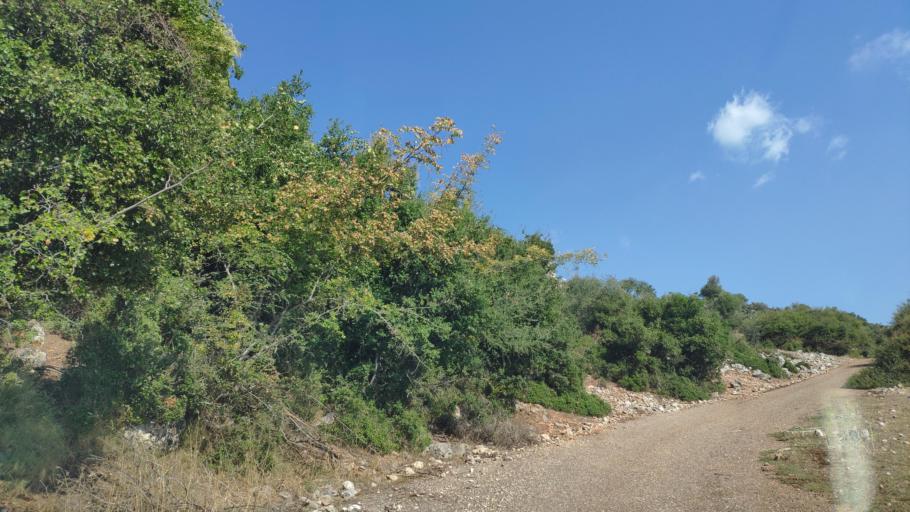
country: GR
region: West Greece
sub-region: Nomos Aitolias kai Akarnanias
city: Fitiai
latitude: 38.6798
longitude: 21.1404
